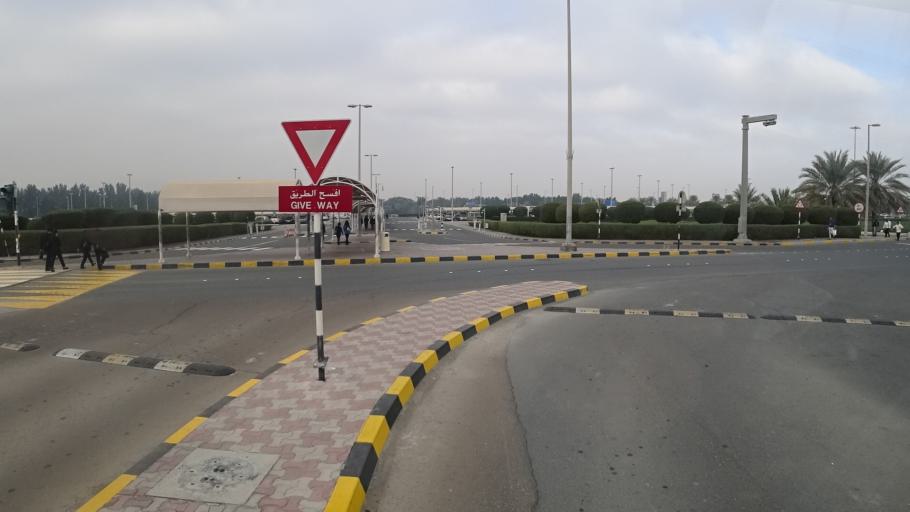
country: AE
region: Abu Dhabi
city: Abu Dhabi
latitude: 24.4256
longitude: 54.6447
